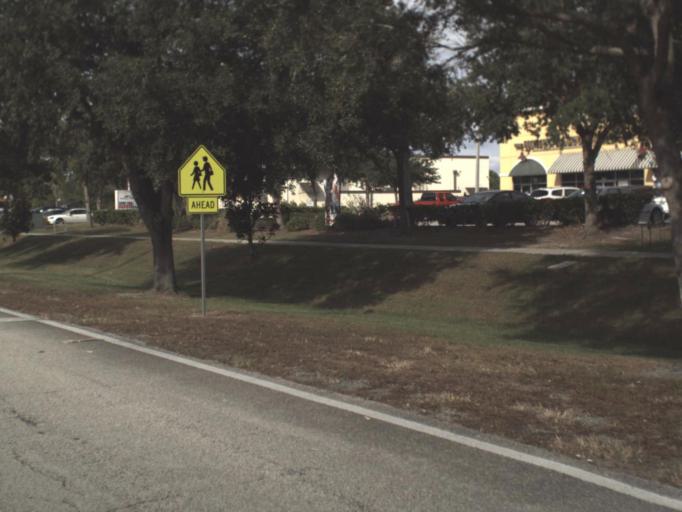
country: US
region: Florida
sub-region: Orange County
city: Hunters Creek
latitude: 28.3667
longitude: -81.4251
